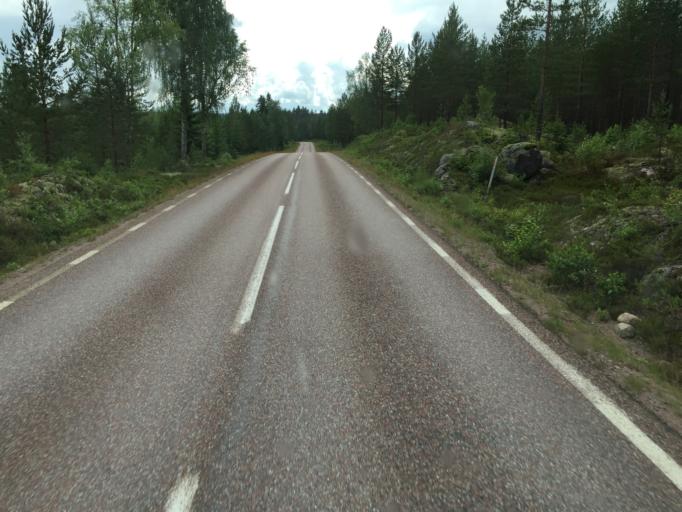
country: SE
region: Dalarna
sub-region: Vansbro Kommun
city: Vansbro
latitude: 60.7306
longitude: 14.1174
